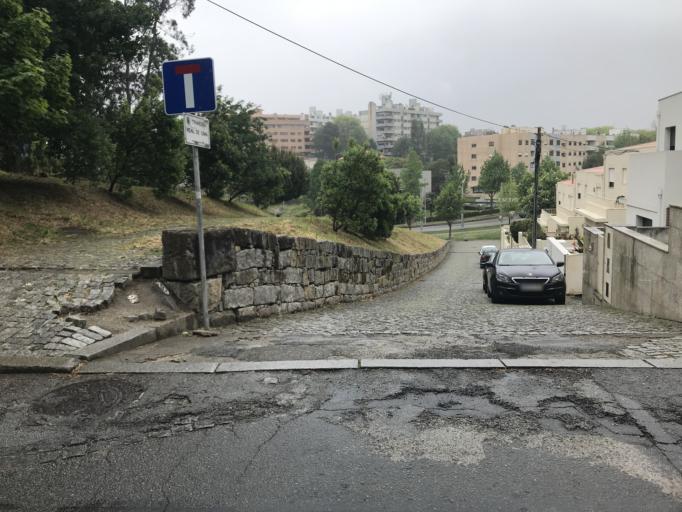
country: PT
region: Porto
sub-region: Matosinhos
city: Senhora da Hora
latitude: 41.1784
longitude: -8.6697
